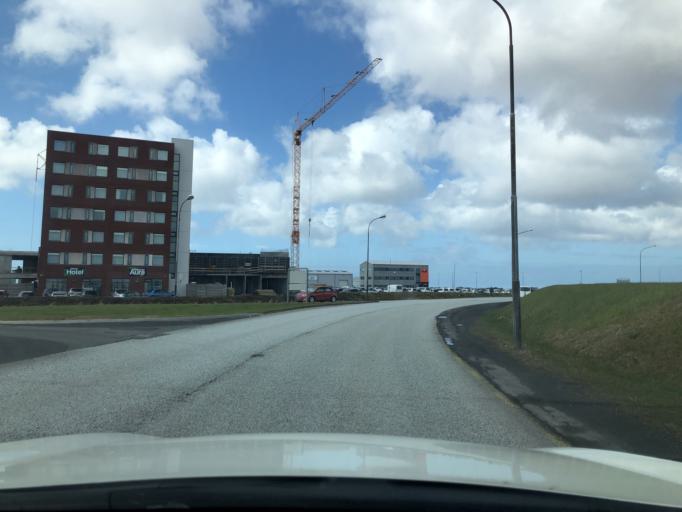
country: IS
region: Southern Peninsula
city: Reykjanesbaer
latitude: 63.9979
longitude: -22.6260
